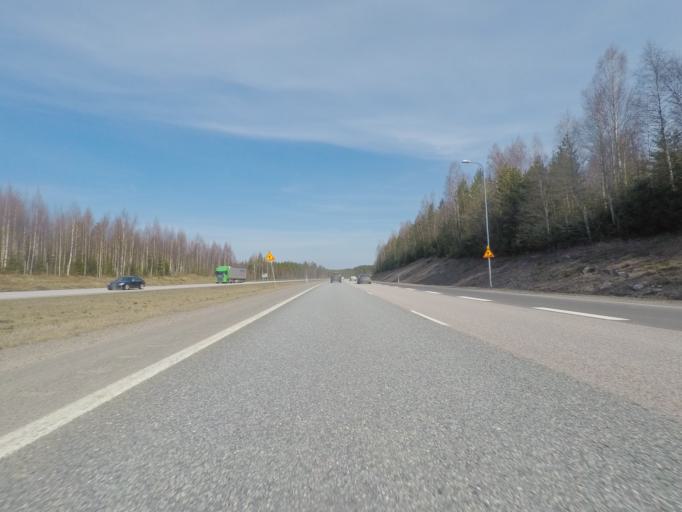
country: FI
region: Paijanne Tavastia
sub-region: Lahti
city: Nastola
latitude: 61.0488
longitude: 25.8535
